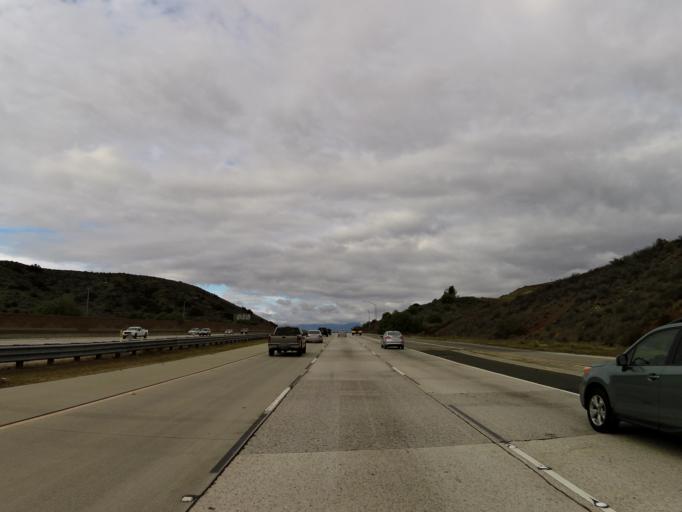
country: US
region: California
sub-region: Ventura County
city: Moorpark
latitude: 34.2686
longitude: -118.8525
